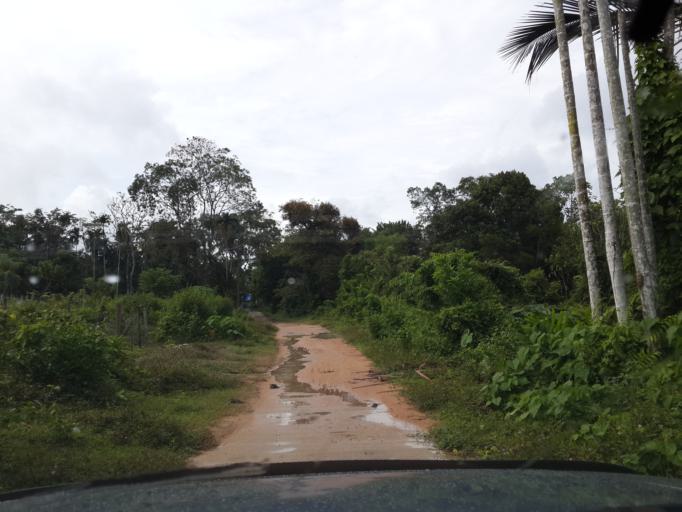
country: TH
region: Narathiwat
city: Rueso
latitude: 6.3816
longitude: 101.5237
